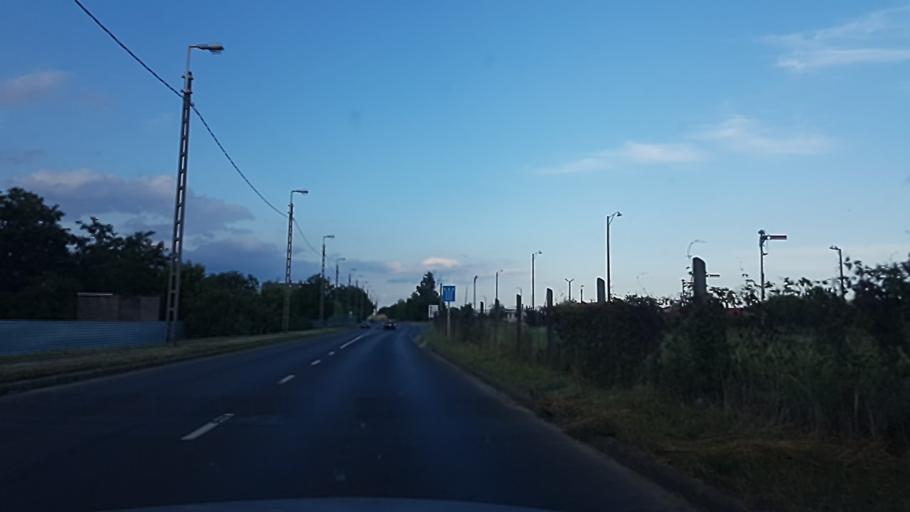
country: HU
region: Baranya
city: Szigetvar
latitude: 46.0431
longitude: 17.8063
